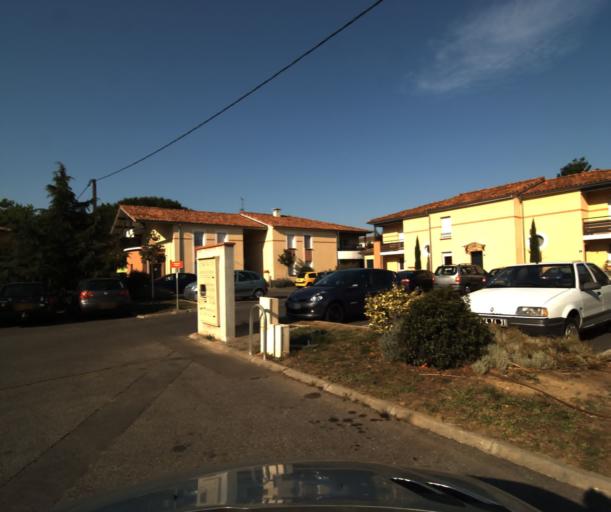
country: FR
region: Midi-Pyrenees
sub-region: Departement de la Haute-Garonne
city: Roquettes
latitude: 43.4826
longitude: 1.3878
